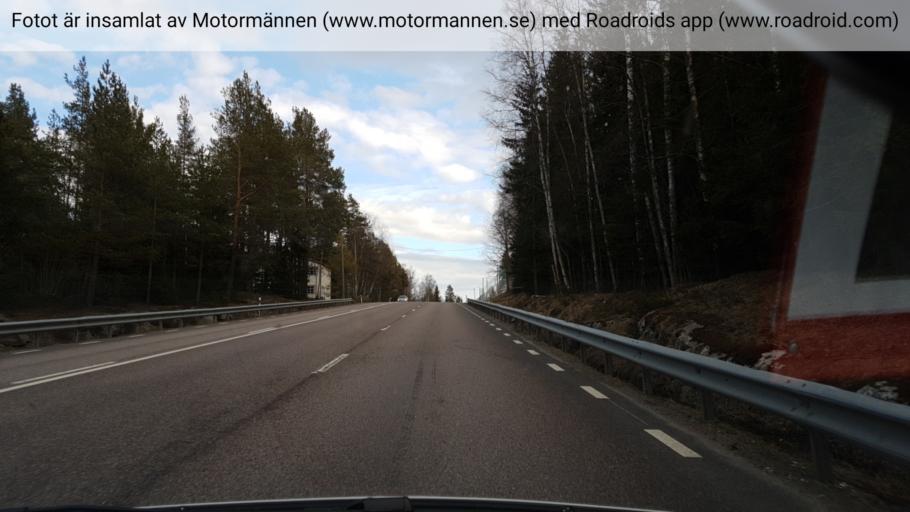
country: SE
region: Vaesternorrland
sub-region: Kramfors Kommun
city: Kramfors
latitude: 62.8160
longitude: 17.8614
